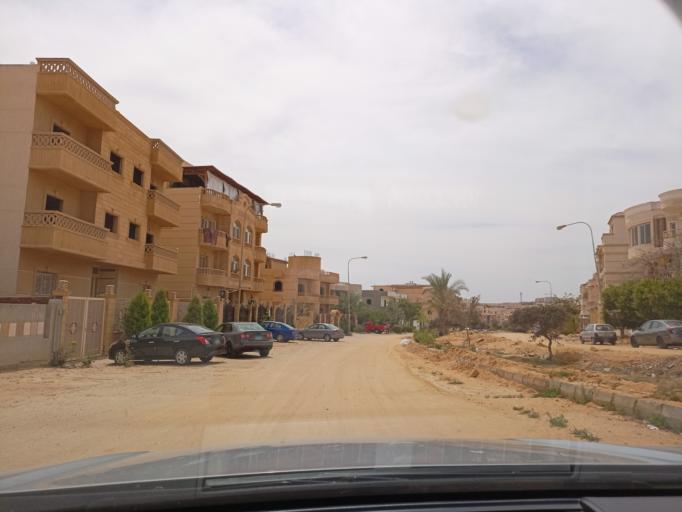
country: EG
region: Muhafazat al Qalyubiyah
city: Al Khankah
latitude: 30.2405
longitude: 31.4965
